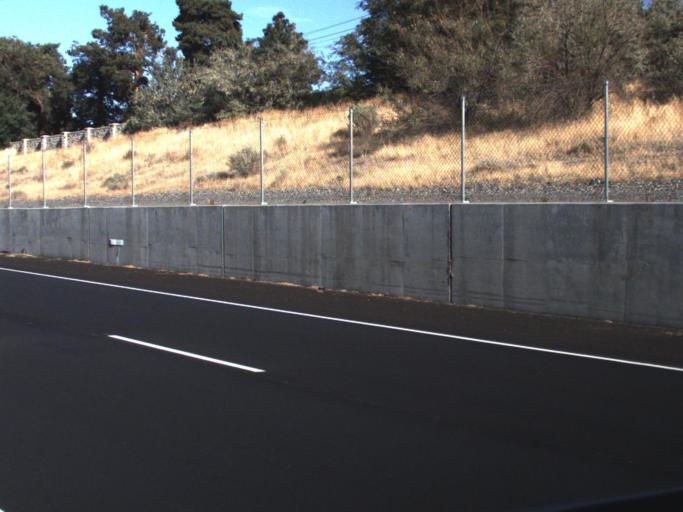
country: US
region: Washington
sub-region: Benton County
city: Richland
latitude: 46.2623
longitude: -119.2924
